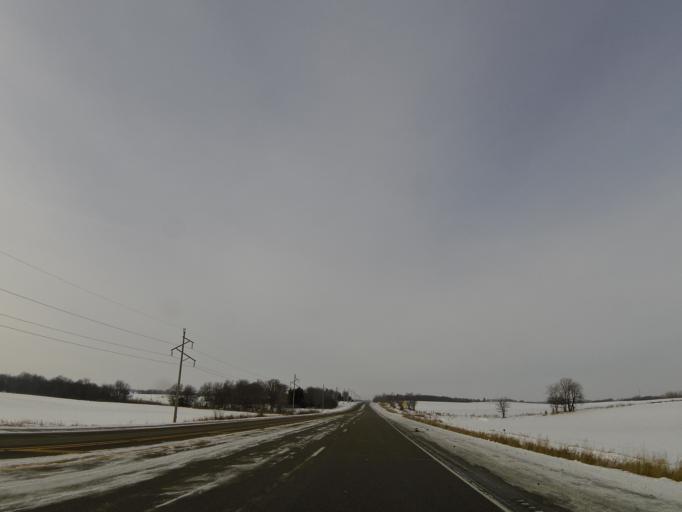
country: US
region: Minnesota
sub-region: Carver County
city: Mayer
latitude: 44.9056
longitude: -93.8415
